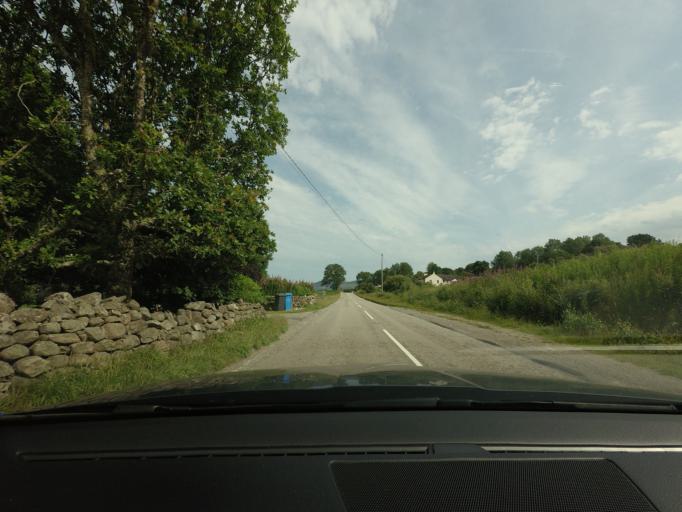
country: GB
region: Scotland
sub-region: Highland
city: Alness
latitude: 57.8710
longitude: -4.3478
